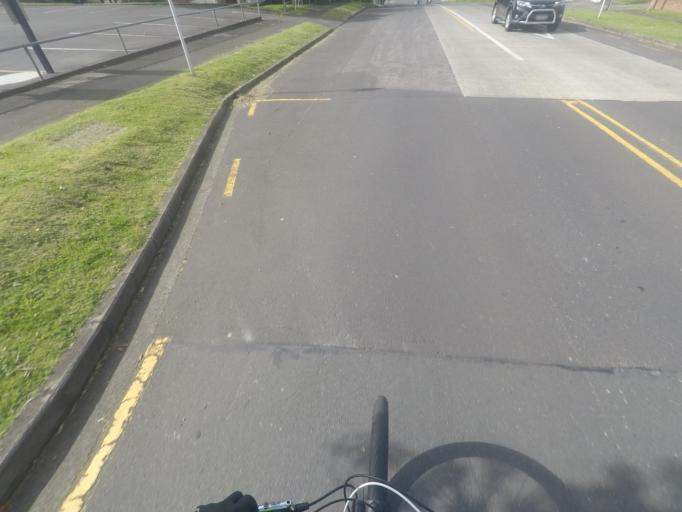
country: NZ
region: Auckland
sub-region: Auckland
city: Mangere
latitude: -36.9197
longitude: 174.7827
